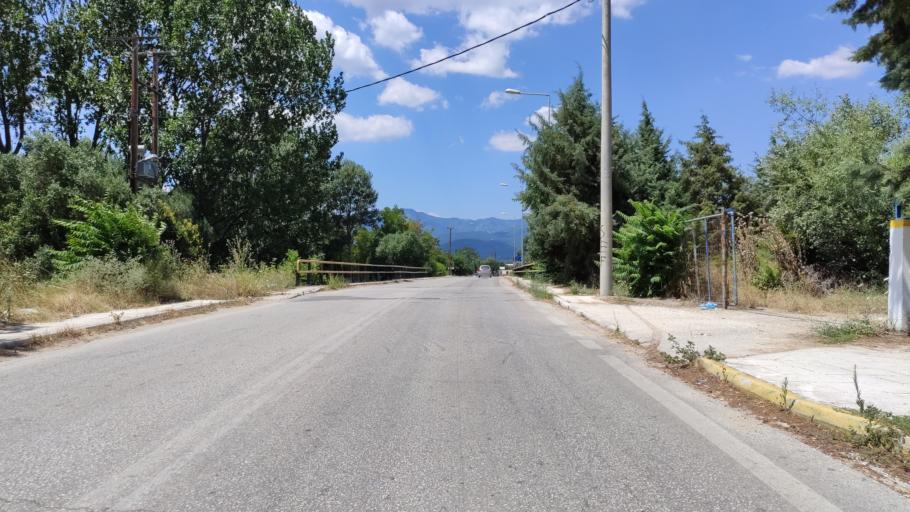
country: GR
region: East Macedonia and Thrace
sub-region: Nomos Rodopis
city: Komotini
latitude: 41.1269
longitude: 25.3856
